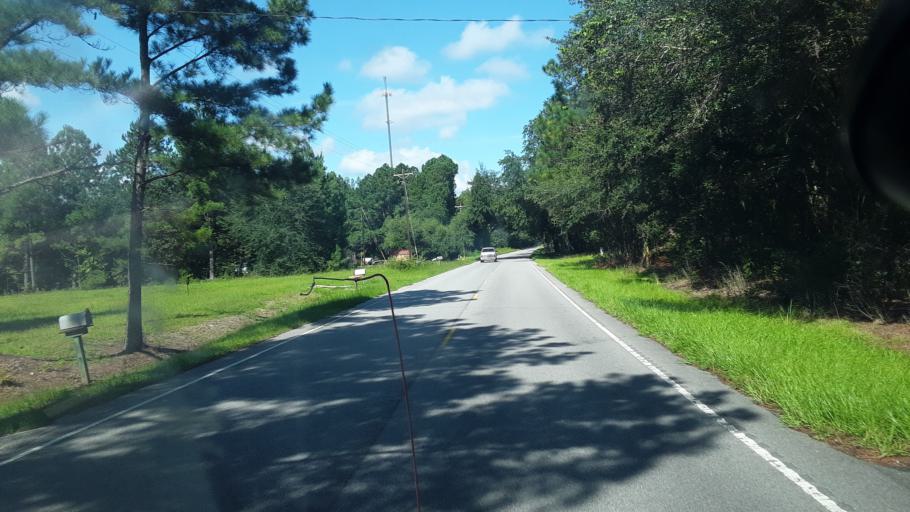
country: US
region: South Carolina
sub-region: Jasper County
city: Ridgeland
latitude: 32.5900
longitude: -80.9630
